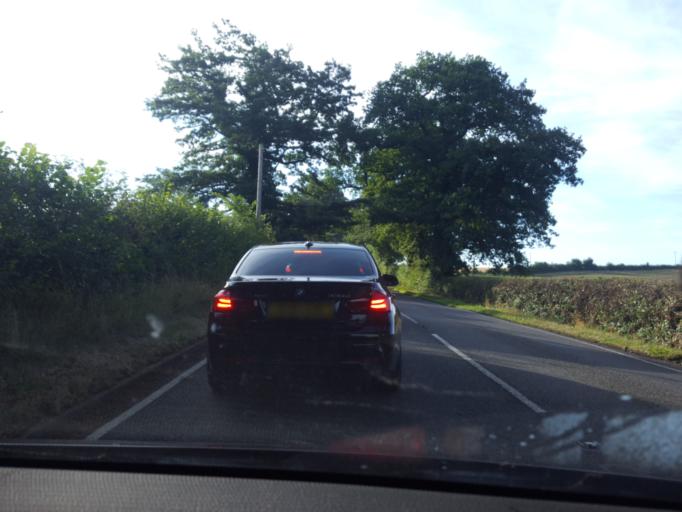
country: GB
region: England
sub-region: Leicestershire
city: Shepshed
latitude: 52.7435
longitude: -1.2730
